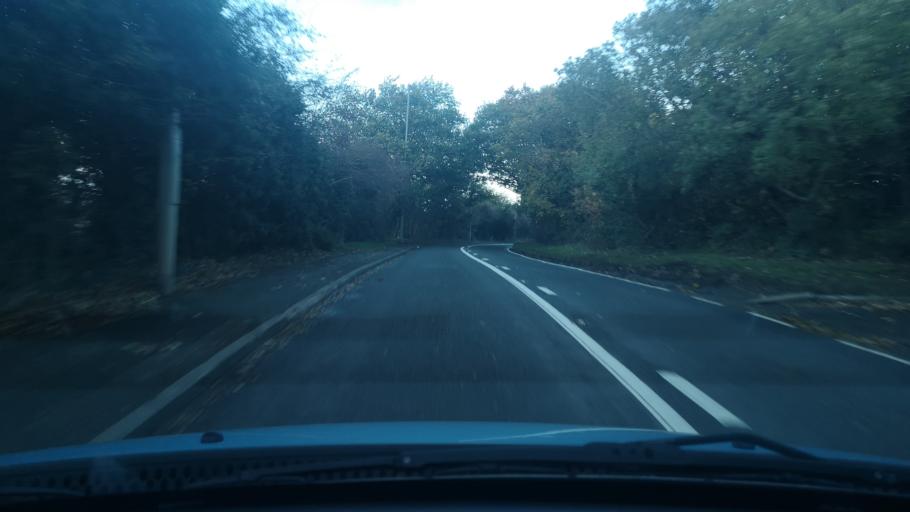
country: GB
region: England
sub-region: City and Borough of Wakefield
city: Middlestown
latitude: 53.6346
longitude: -1.5865
